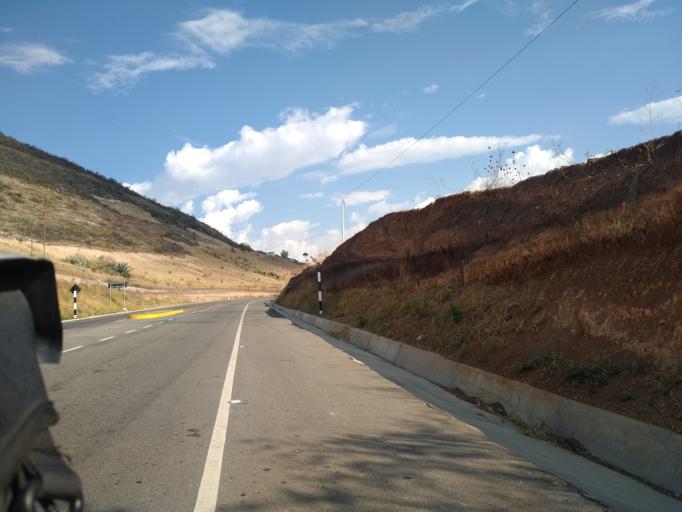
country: PE
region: Cajamarca
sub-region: San Marcos
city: San Marcos
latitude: -7.3793
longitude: -78.1258
